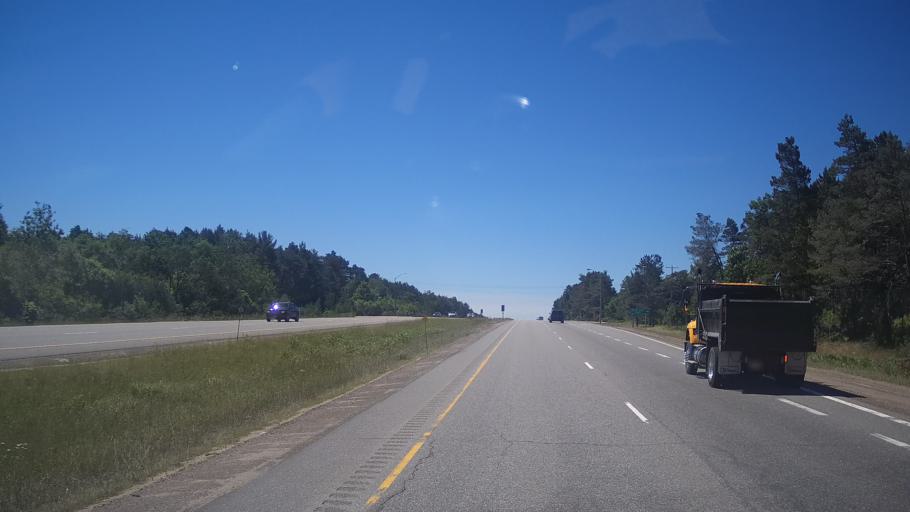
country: CA
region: Ontario
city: Bracebridge
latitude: 45.0745
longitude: -79.2969
